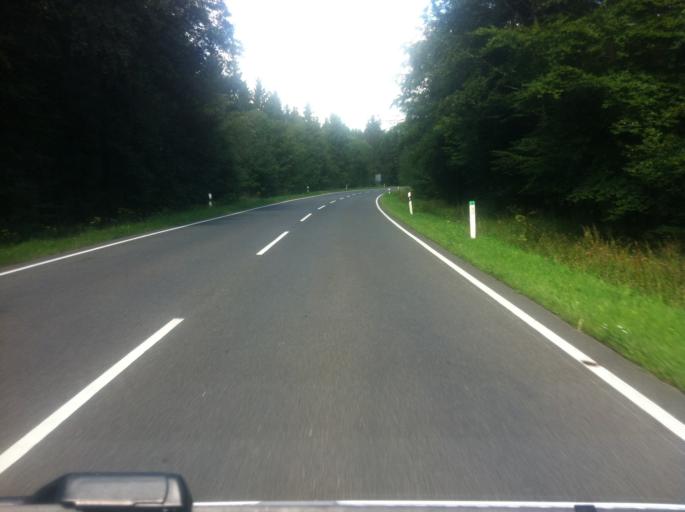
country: DE
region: Rheinland-Pfalz
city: Scheid
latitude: 50.3840
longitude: 6.3460
